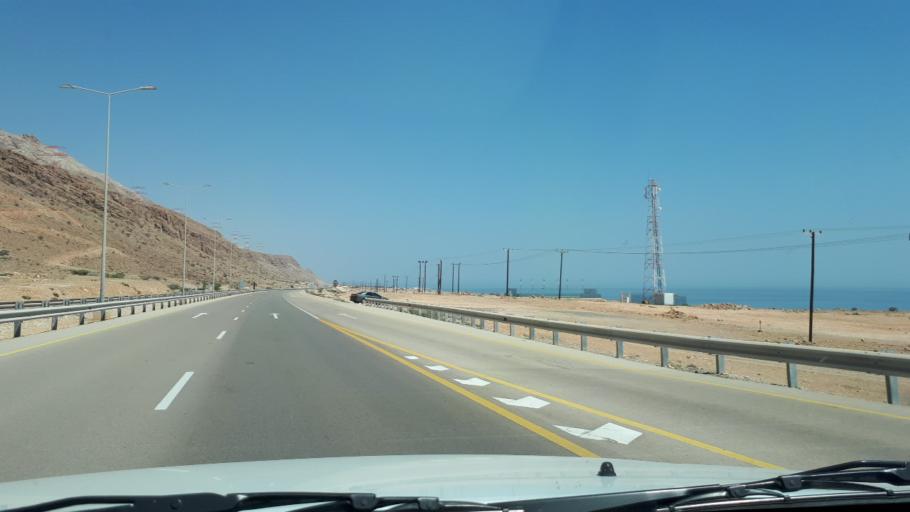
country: OM
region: Ash Sharqiyah
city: Sur
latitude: 22.7899
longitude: 59.2755
